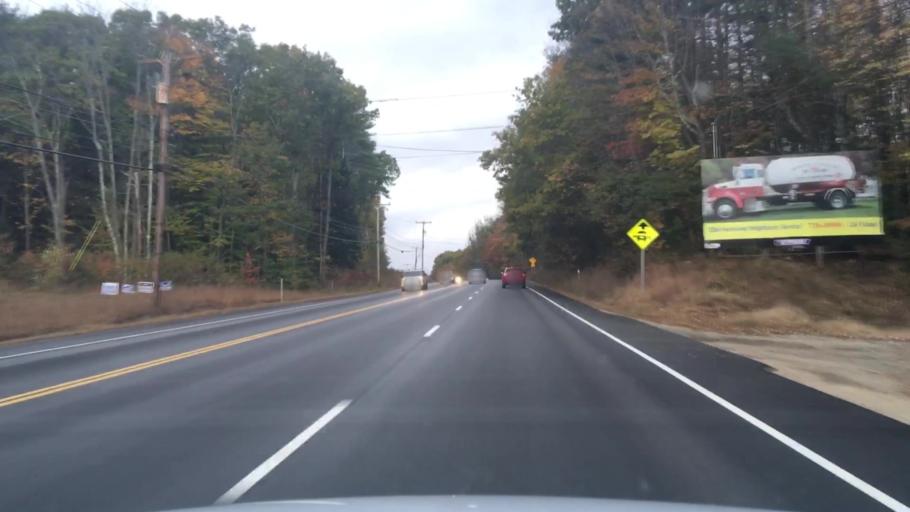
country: US
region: New Hampshire
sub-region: Merrimack County
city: Chichester
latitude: 43.2360
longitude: -71.3871
